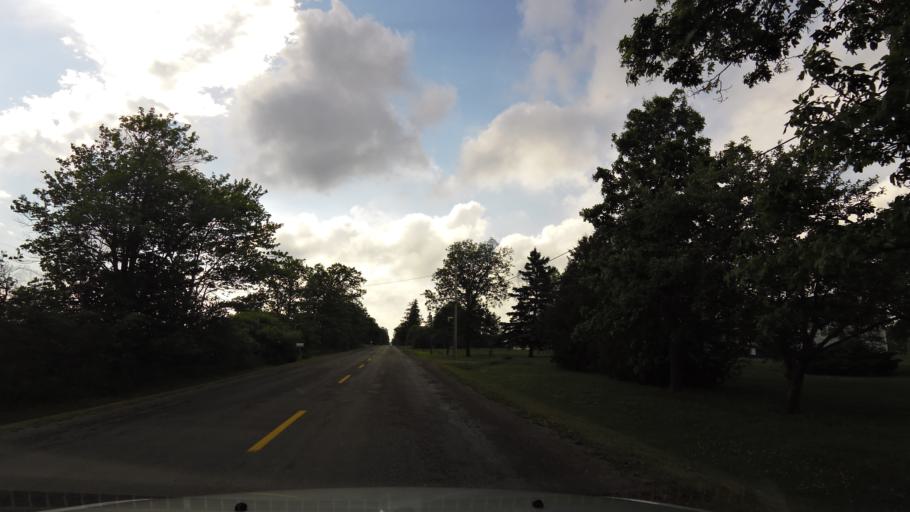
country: CA
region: Ontario
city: Ancaster
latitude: 43.0106
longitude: -80.0725
